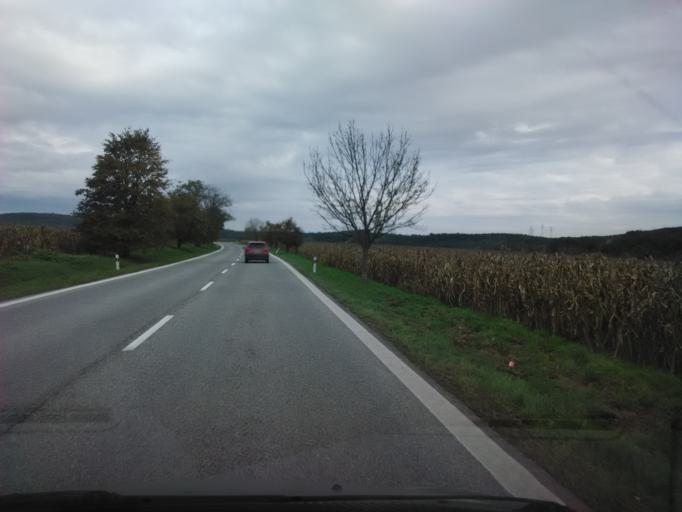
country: SK
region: Nitriansky
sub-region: Okres Nitra
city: Vrable
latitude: 48.2313
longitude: 18.4003
